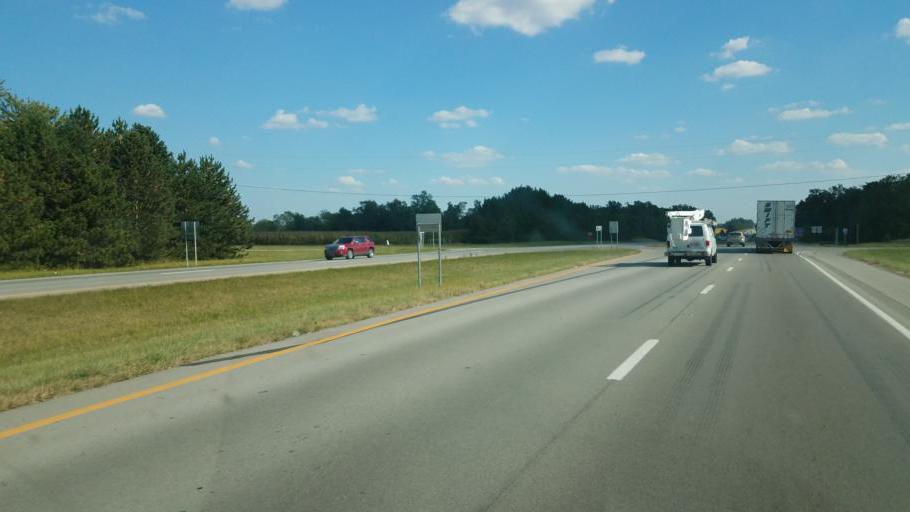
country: US
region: Ohio
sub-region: Wyandot County
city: Upper Sandusky
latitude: 40.8538
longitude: -83.2654
